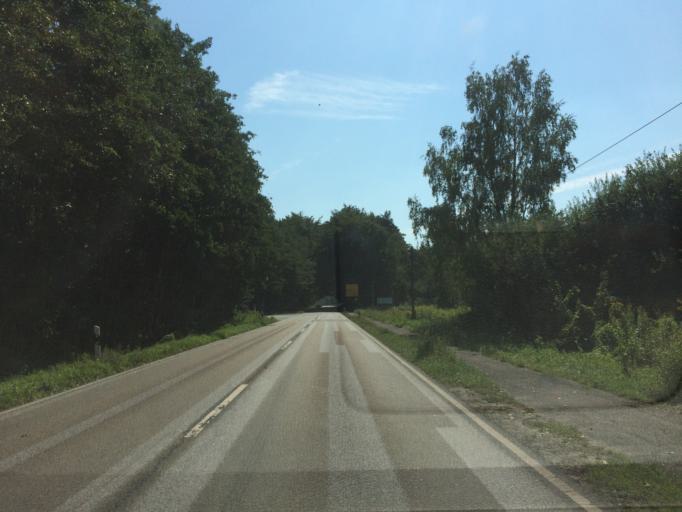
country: DE
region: North Rhine-Westphalia
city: Marl
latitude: 51.6584
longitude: 7.0334
